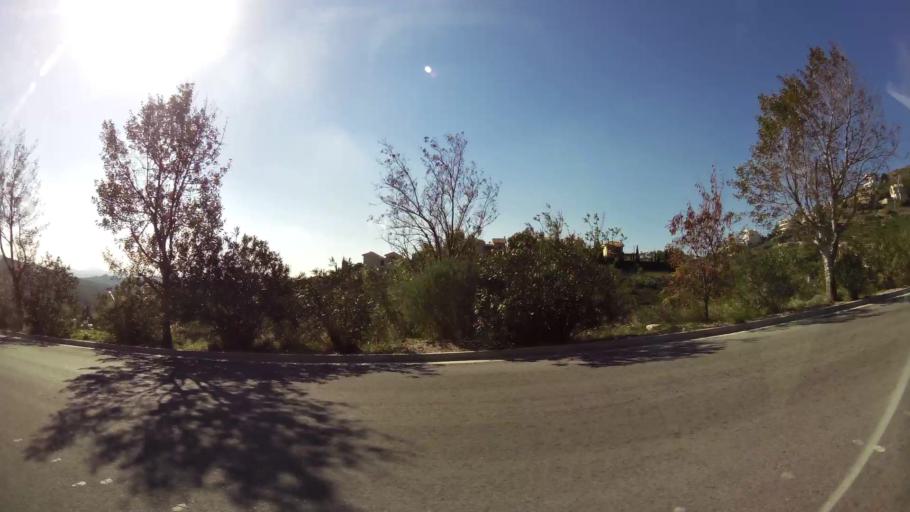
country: GR
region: Attica
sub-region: Nomarchia Anatolikis Attikis
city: Dhrafi
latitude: 38.0404
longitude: 23.9011
